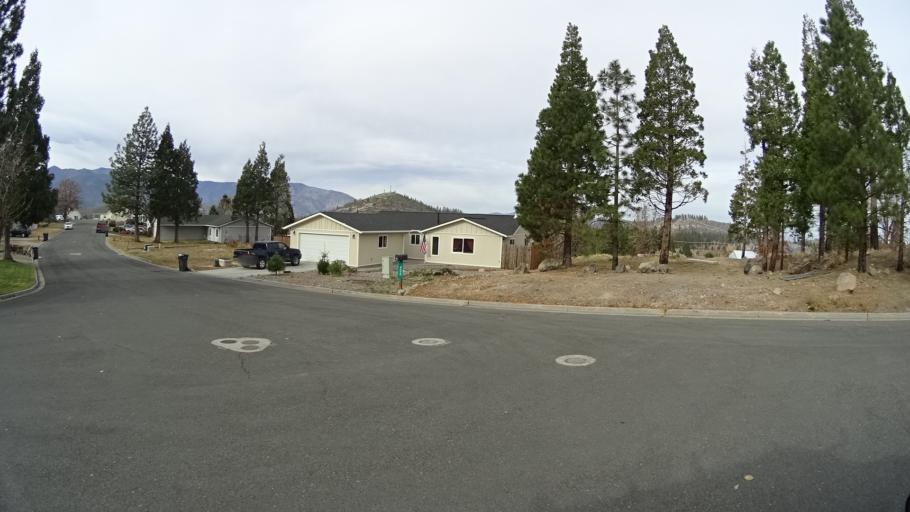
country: US
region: California
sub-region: Siskiyou County
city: Weed
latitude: 41.4301
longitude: -122.3804
